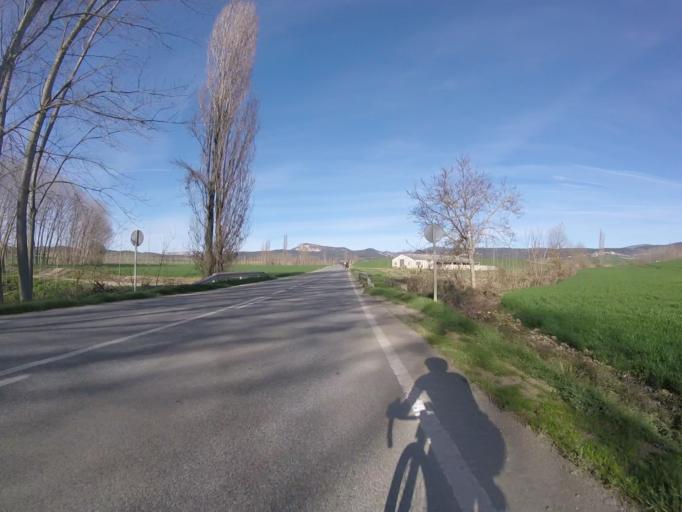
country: ES
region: Navarre
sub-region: Provincia de Navarra
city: Yerri
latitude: 42.7176
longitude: -1.9873
